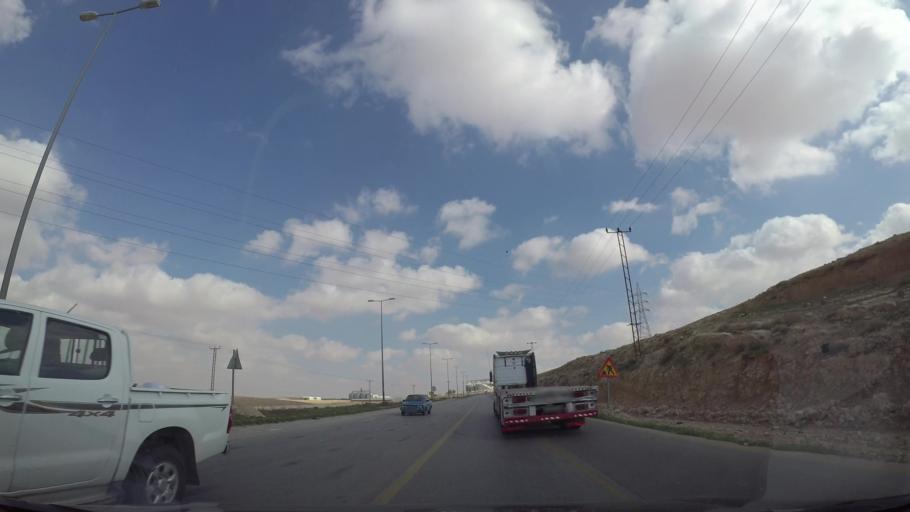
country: JO
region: Amman
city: Al Jizah
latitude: 31.6275
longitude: 35.9895
